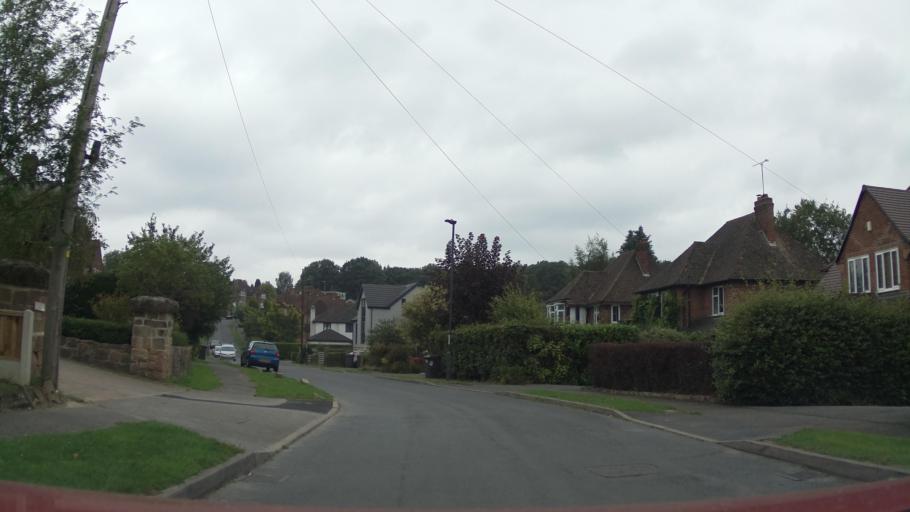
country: GB
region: England
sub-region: Derbyshire
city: Little Eaton
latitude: 52.9584
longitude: -1.4785
